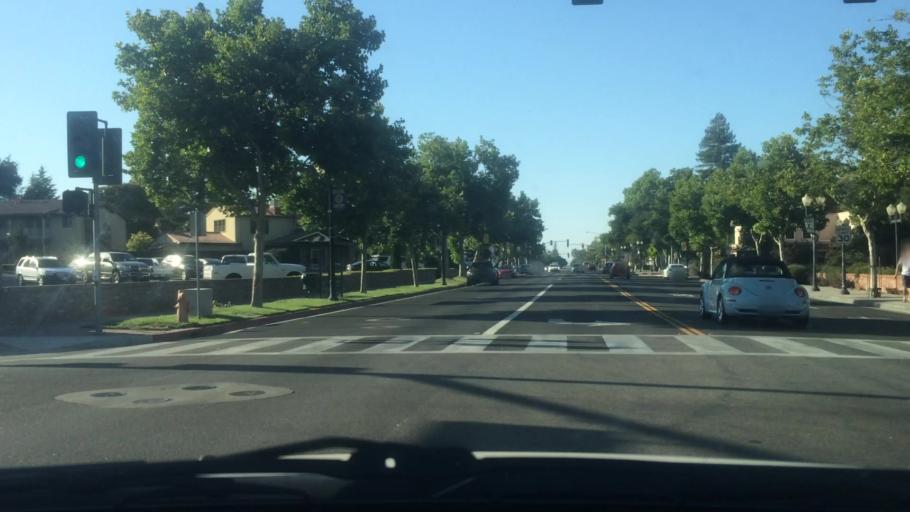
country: US
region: California
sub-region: San Luis Obispo County
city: Paso Robles
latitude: 35.6246
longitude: -120.6913
